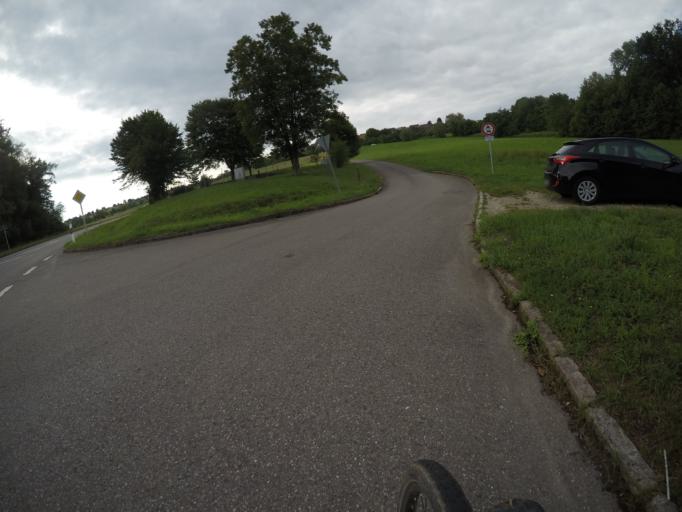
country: DE
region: Baden-Wuerttemberg
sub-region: Regierungsbezirk Stuttgart
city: Schlaitdorf
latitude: 48.5984
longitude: 9.2276
